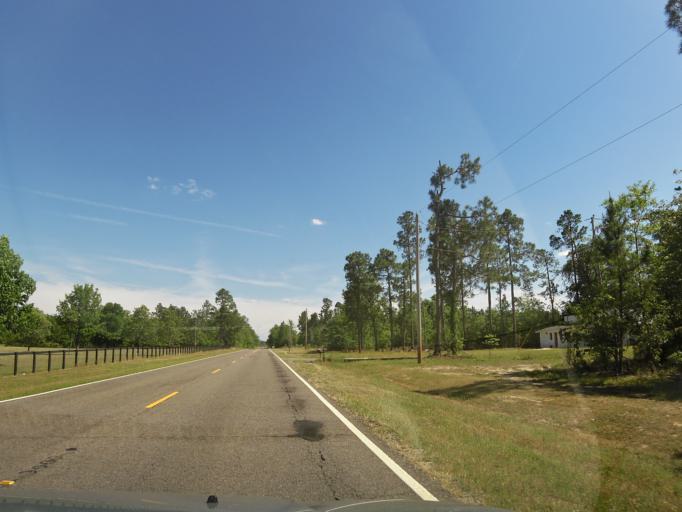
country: US
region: South Carolina
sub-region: Barnwell County
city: Williston
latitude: 33.4673
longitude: -81.5038
